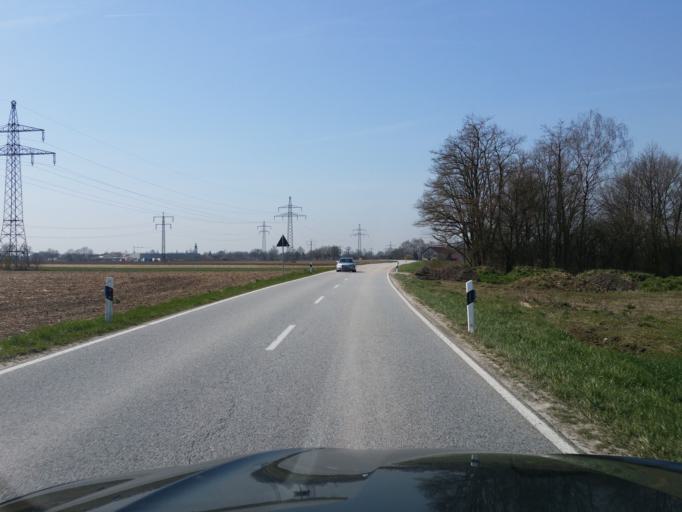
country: DE
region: Bavaria
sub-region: Upper Bavaria
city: Langenpreising
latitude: 48.4382
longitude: 11.9848
